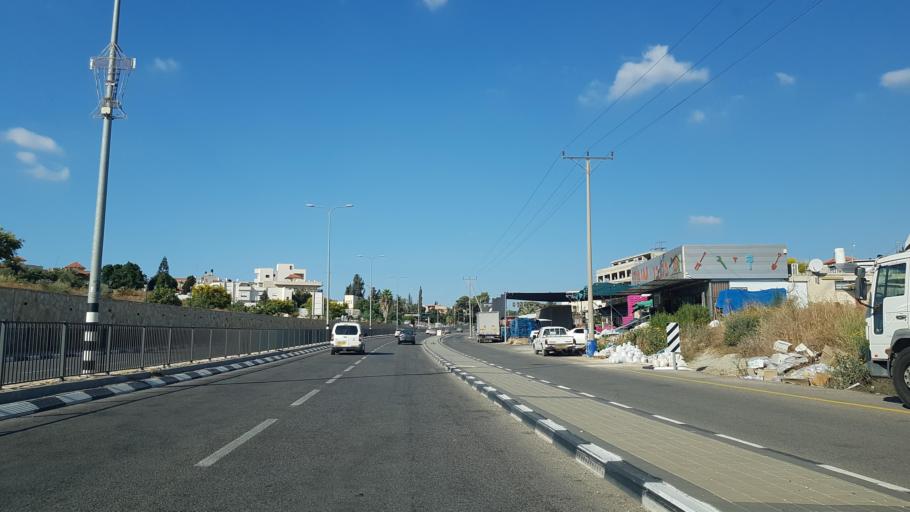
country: PS
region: West Bank
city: Zayta
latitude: 32.3637
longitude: 35.0307
